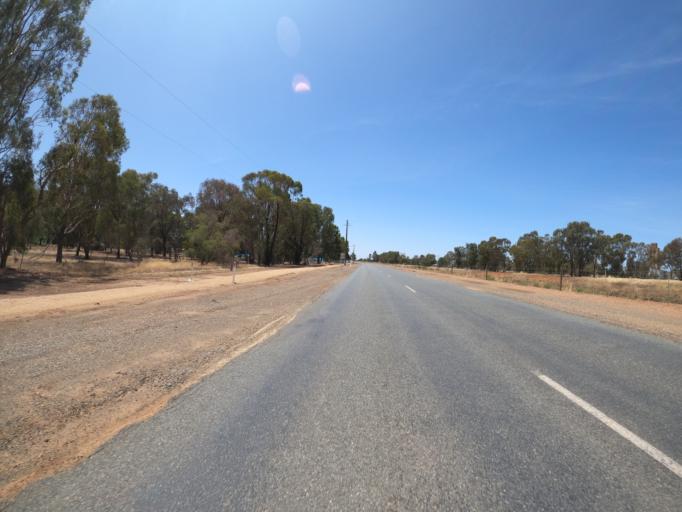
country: AU
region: Victoria
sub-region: Moira
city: Yarrawonga
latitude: -36.0153
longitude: 145.9965
